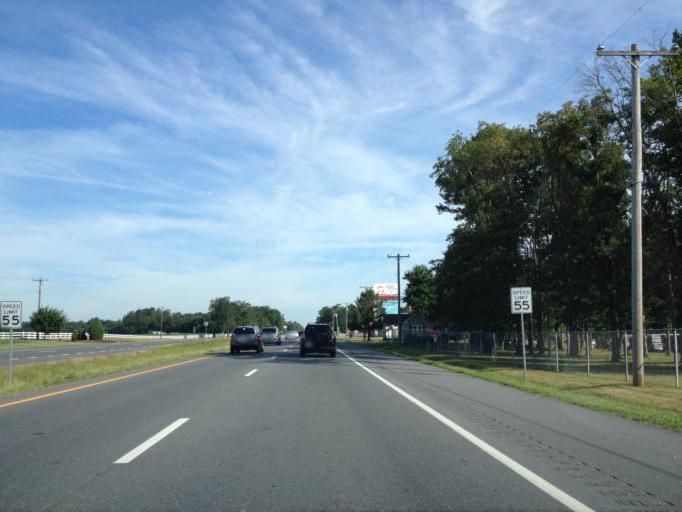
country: US
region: Delaware
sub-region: Sussex County
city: Georgetown
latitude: 38.6355
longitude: -75.3514
